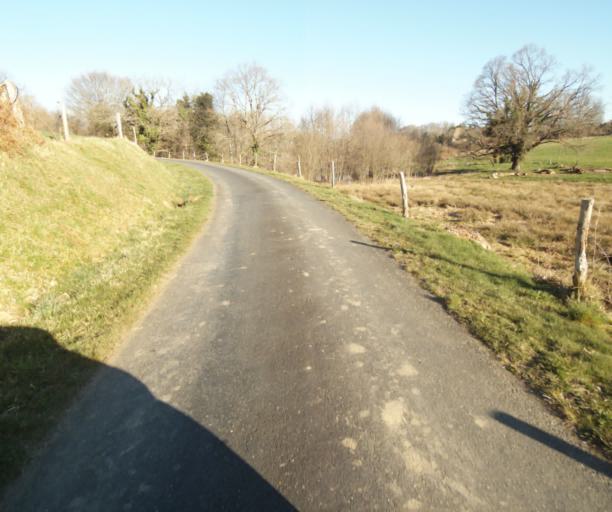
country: FR
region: Limousin
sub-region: Departement de la Correze
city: Uzerche
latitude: 45.3755
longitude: 1.5773
